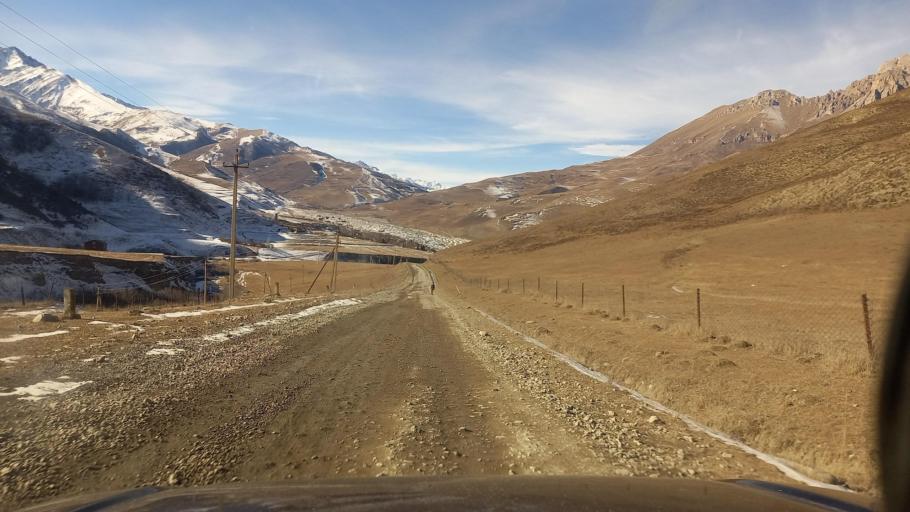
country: RU
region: North Ossetia
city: Verkhniy Fiagdon
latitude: 42.8391
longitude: 44.4573
